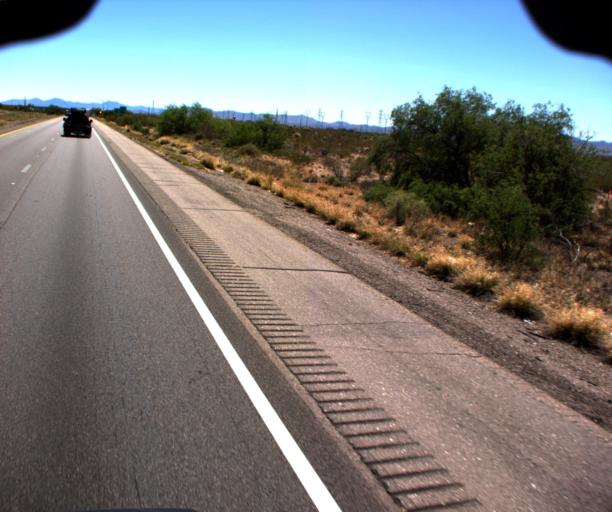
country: US
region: Arizona
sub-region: Pima County
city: Vail
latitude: 32.0653
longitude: -110.7799
